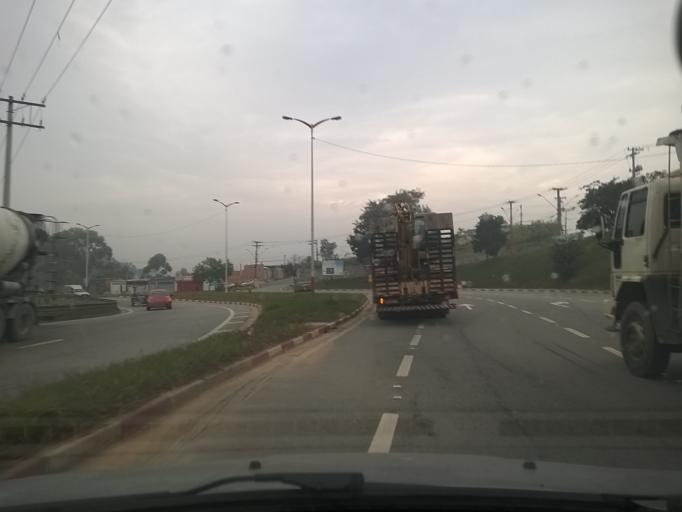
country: BR
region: Sao Paulo
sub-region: Caieiras
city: Caieiras
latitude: -23.3810
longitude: -46.7377
